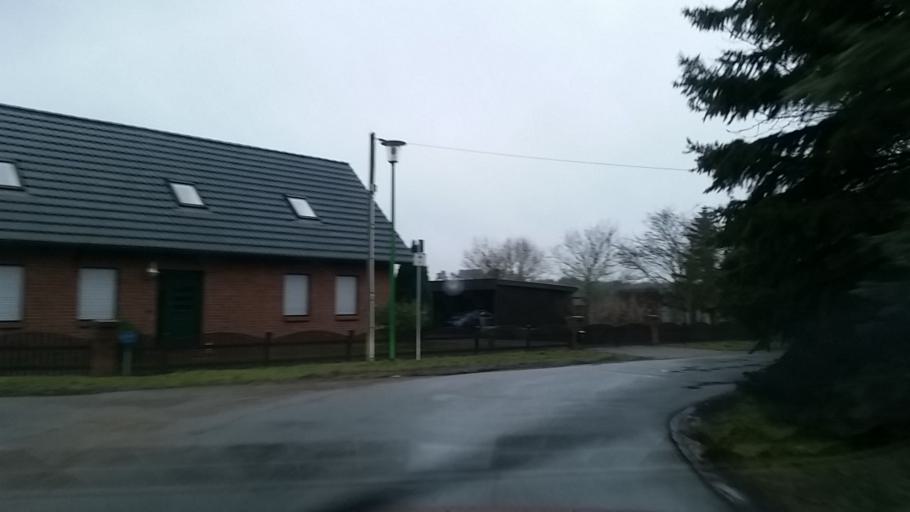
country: DE
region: Brandenburg
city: Gumtow
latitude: 53.0009
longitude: 12.2199
